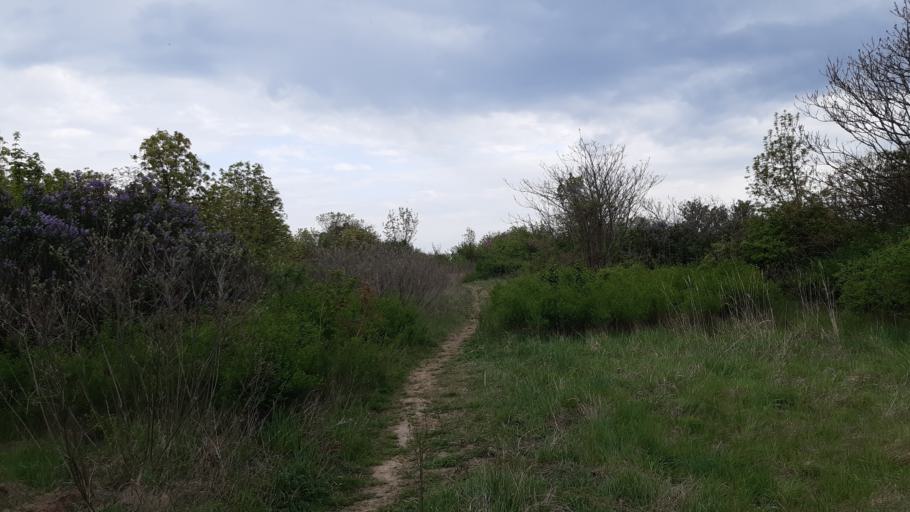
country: HU
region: Budapest
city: Budapest XII. keruelet
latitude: 47.4591
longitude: 19.0036
